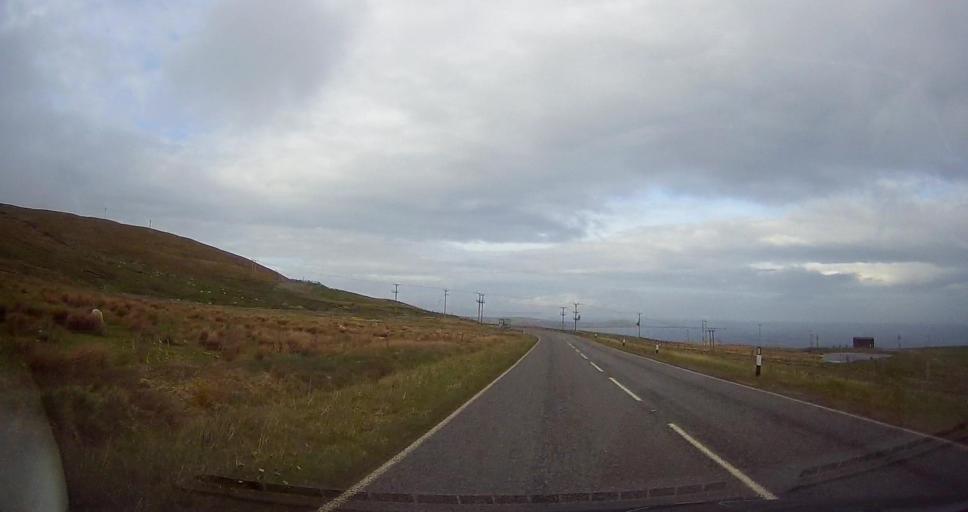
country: GB
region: Scotland
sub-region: Shetland Islands
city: Sandwick
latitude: 60.0151
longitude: -1.2347
